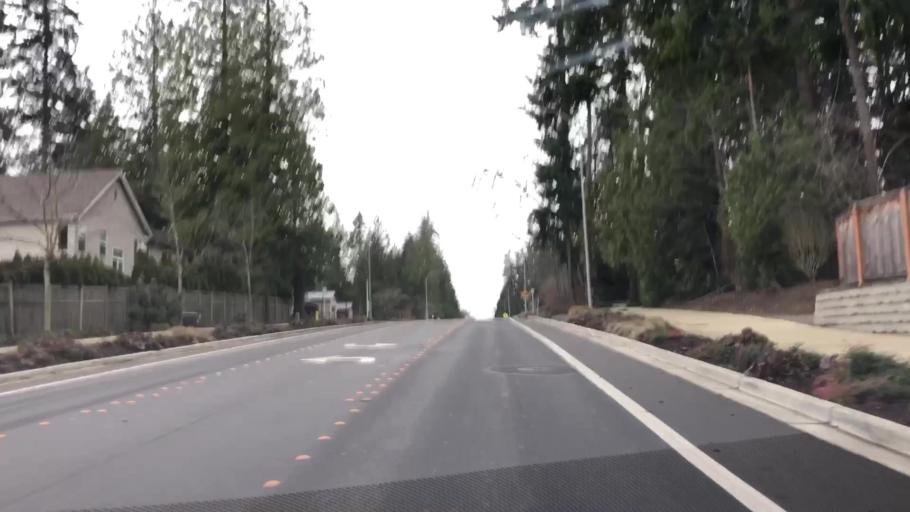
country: US
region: Washington
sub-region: King County
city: Redmond
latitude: 47.7039
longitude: -122.1120
